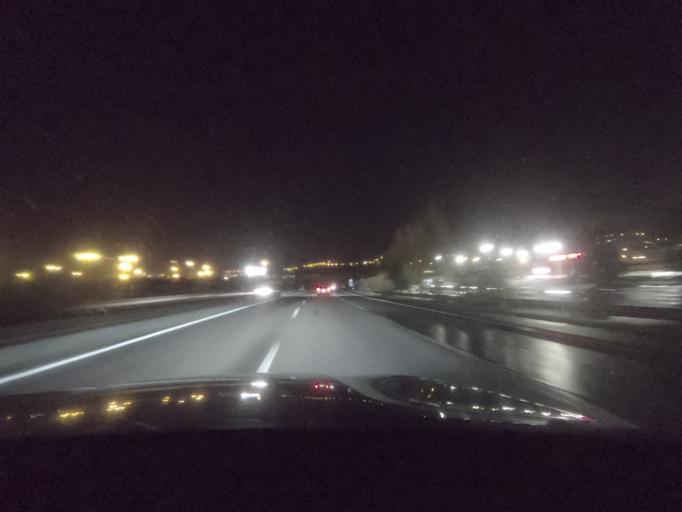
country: PT
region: Porto
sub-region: Paredes
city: Casteloes de Cepeda
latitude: 41.1988
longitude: -8.3363
